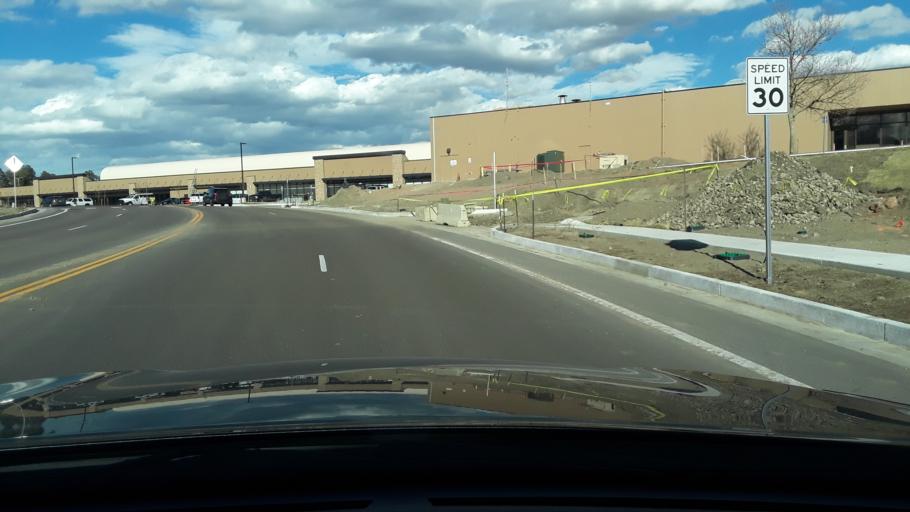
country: US
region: Colorado
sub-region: El Paso County
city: Air Force Academy
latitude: 38.9294
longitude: -104.8087
